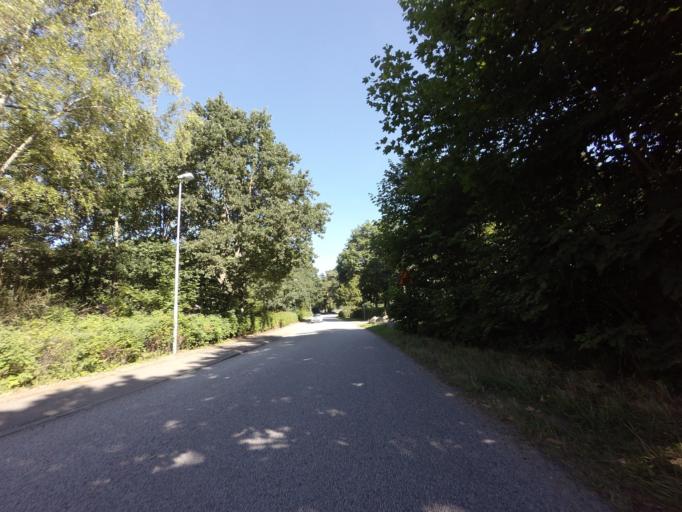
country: SE
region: Skane
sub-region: Ystads Kommun
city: Ystad
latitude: 55.4286
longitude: 13.8488
